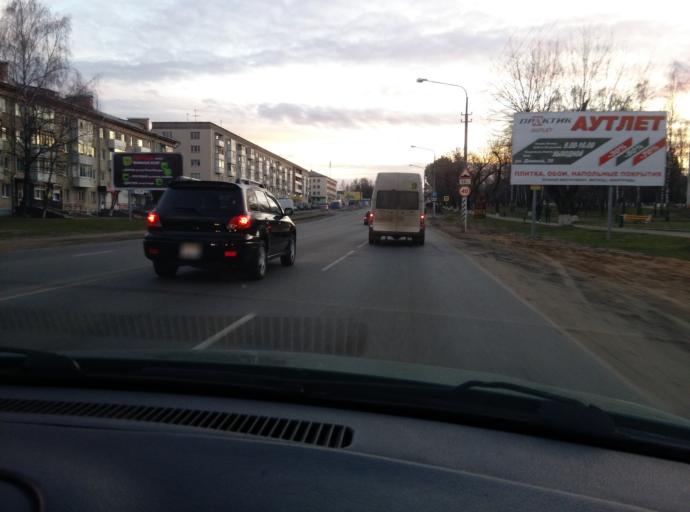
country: BY
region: Minsk
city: Horad Barysaw
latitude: 54.2166
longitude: 28.4898
